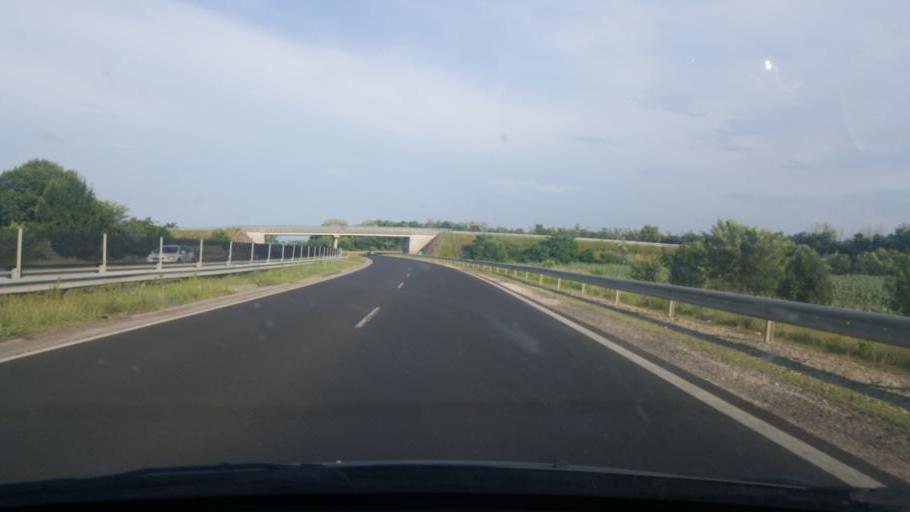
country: HU
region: Pest
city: Vecses
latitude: 47.4163
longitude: 19.2801
